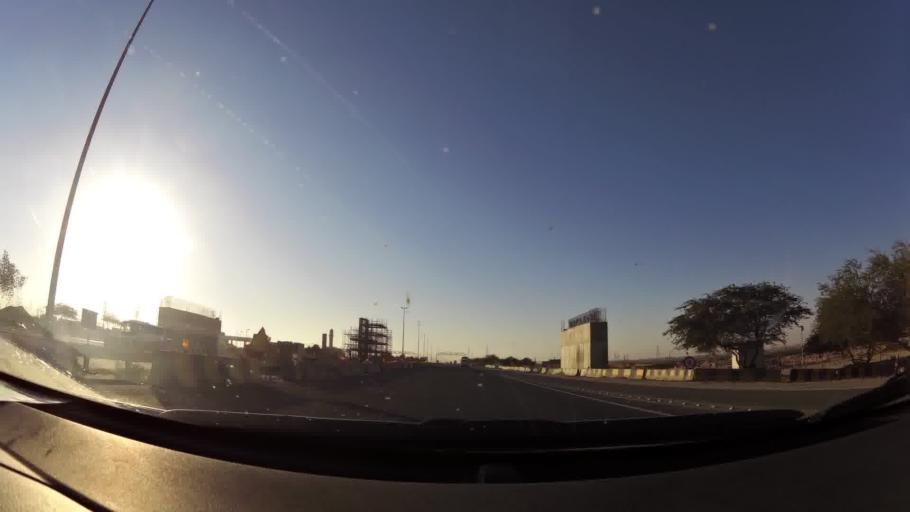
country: KW
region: Al Ahmadi
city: Al Wafrah
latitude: 28.7471
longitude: 48.2825
